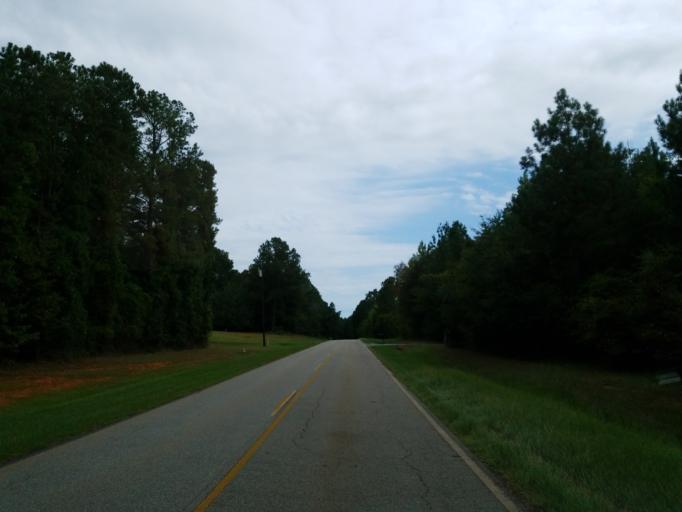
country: US
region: Georgia
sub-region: Monroe County
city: Forsyth
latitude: 32.9157
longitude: -83.9134
